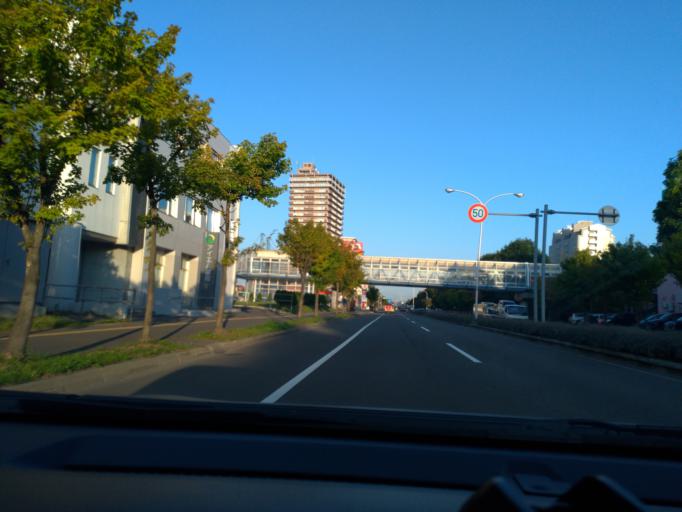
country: JP
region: Hokkaido
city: Ishikari
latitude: 43.1582
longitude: 141.3982
